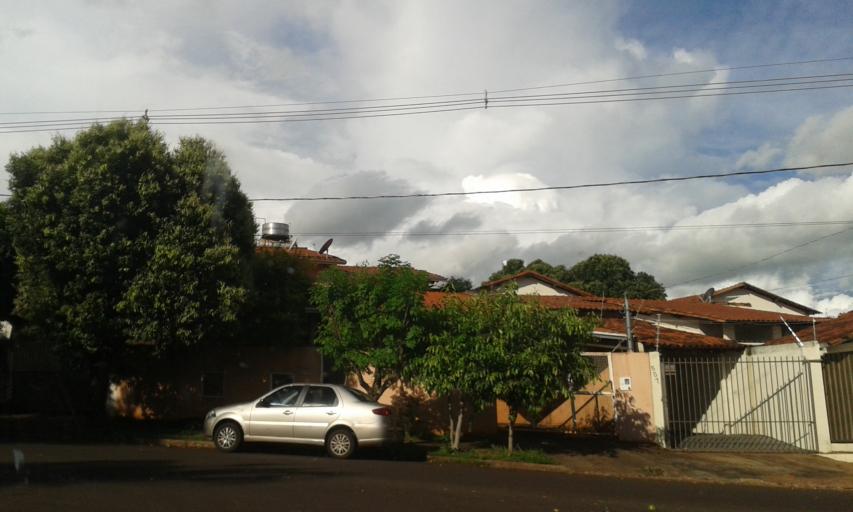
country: BR
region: Minas Gerais
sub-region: Ituiutaba
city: Ituiutaba
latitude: -18.9709
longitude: -49.4516
